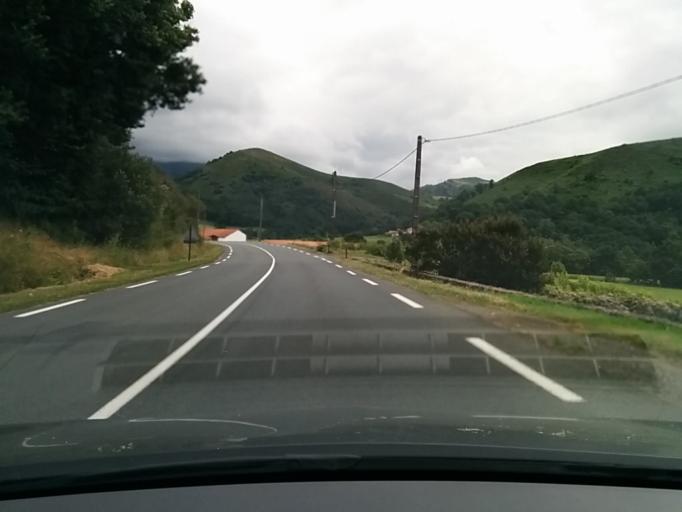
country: FR
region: Aquitaine
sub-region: Departement des Pyrenees-Atlantiques
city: Itxassou
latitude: 43.3056
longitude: -1.3600
